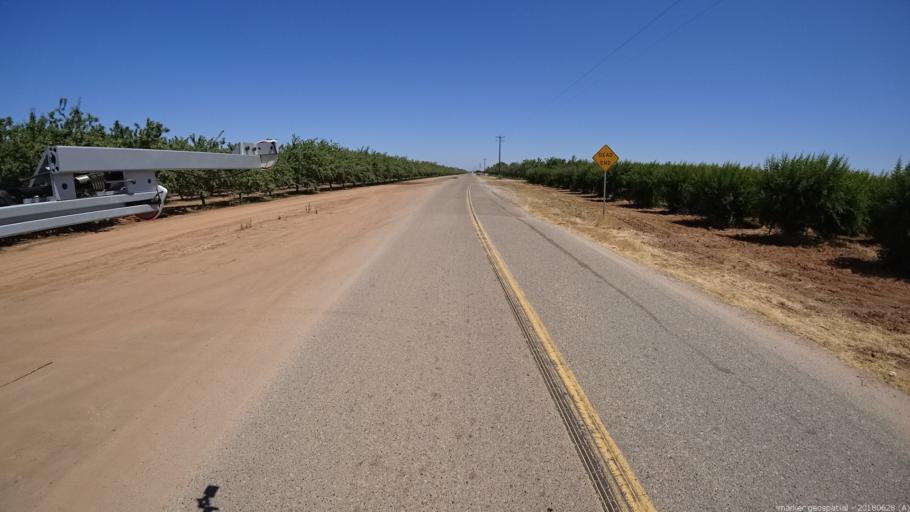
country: US
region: California
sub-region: Madera County
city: Parksdale
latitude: 36.9234
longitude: -119.9471
